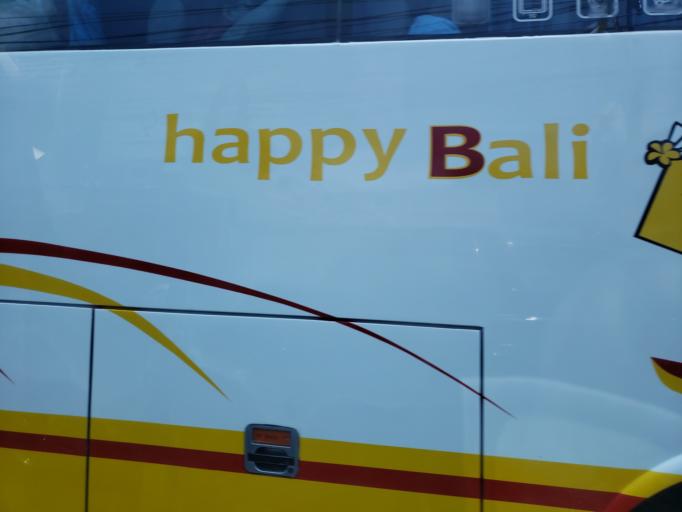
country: ID
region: Bali
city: Jimbaran
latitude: -8.8155
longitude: 115.1562
